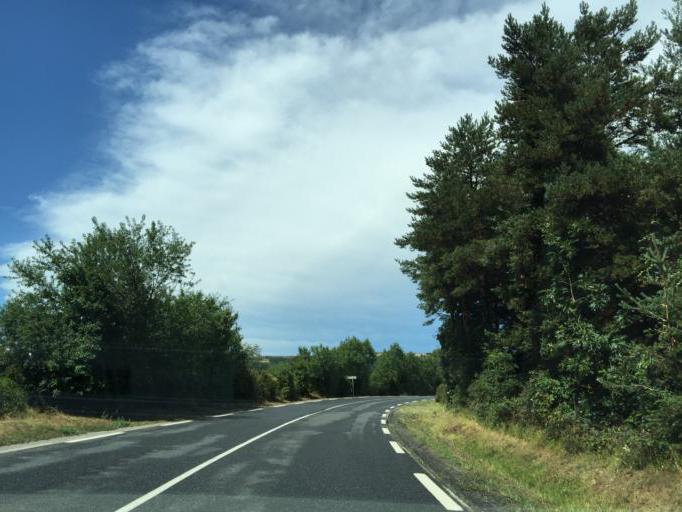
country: FR
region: Midi-Pyrenees
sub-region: Departement de l'Aveyron
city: Severac-le-Chateau
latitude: 44.2266
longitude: 2.9876
